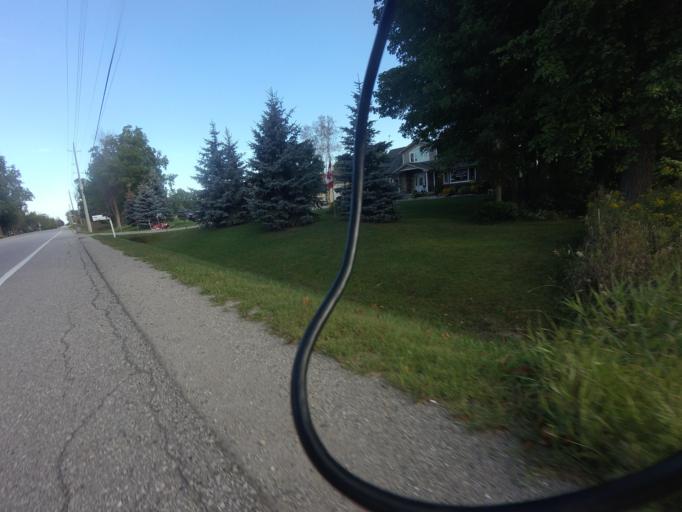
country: CA
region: Ontario
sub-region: Wellington County
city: Guelph
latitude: 43.5751
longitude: -80.3290
